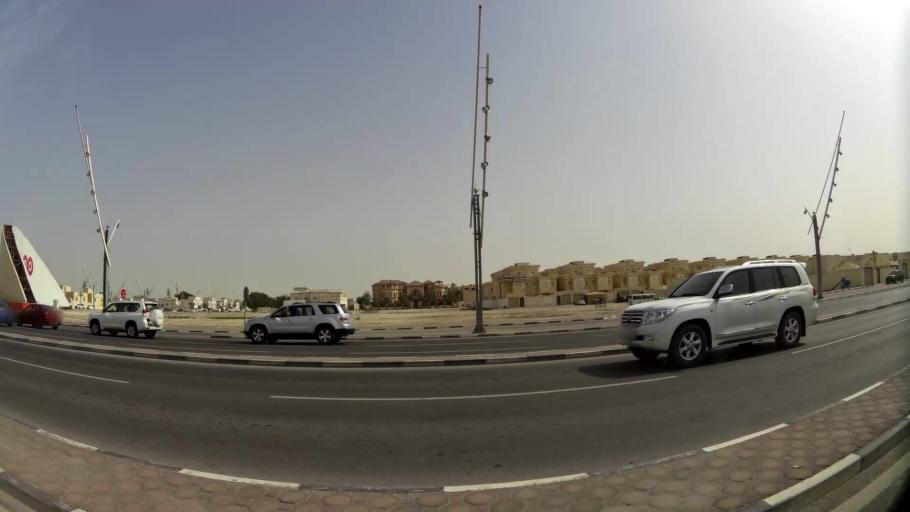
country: QA
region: Baladiyat ad Dawhah
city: Doha
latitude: 25.2692
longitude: 51.4745
